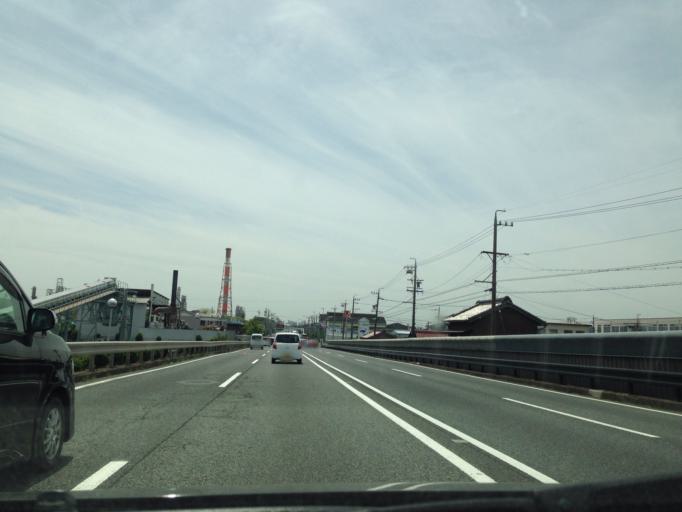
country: JP
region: Mie
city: Yokkaichi
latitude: 34.9774
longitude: 136.6431
